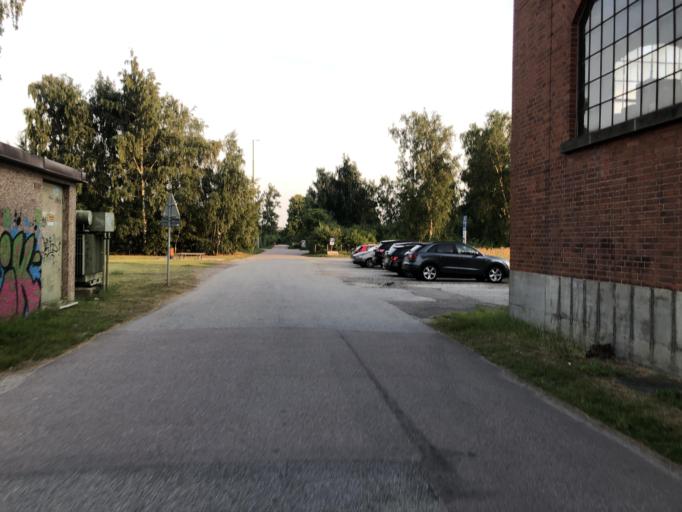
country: SE
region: Skane
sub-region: Burlovs Kommun
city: Arloev
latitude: 55.6053
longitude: 13.0438
